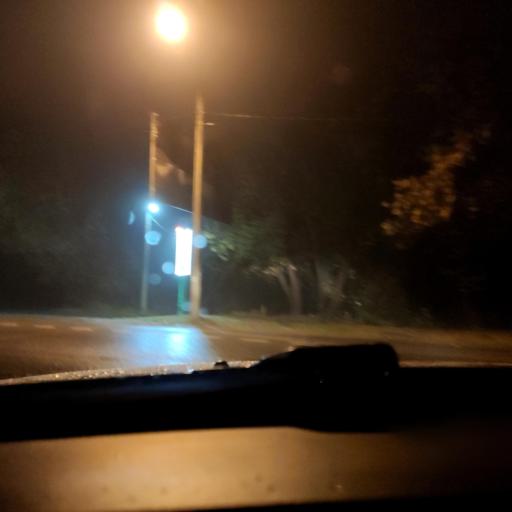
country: RU
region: Voronezj
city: Voronezh
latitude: 51.6195
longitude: 39.1764
